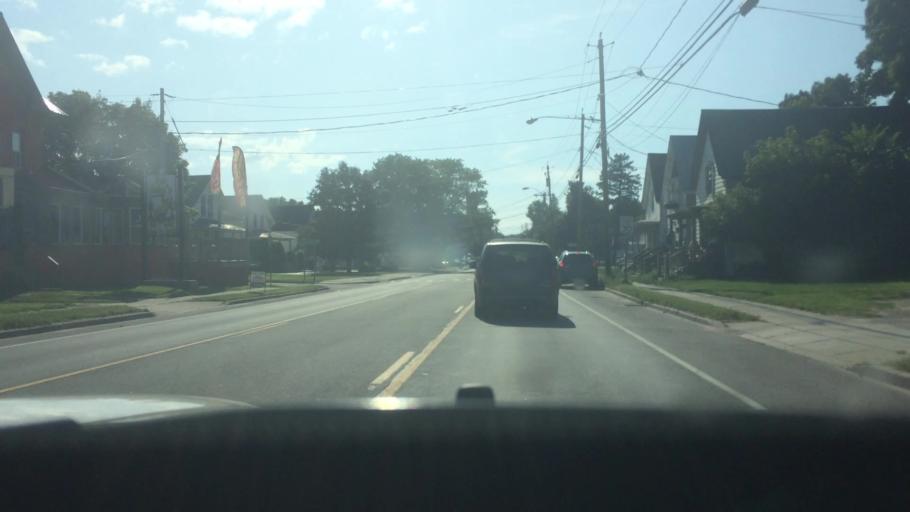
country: US
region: New York
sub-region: Franklin County
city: Malone
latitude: 44.8500
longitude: -74.2812
